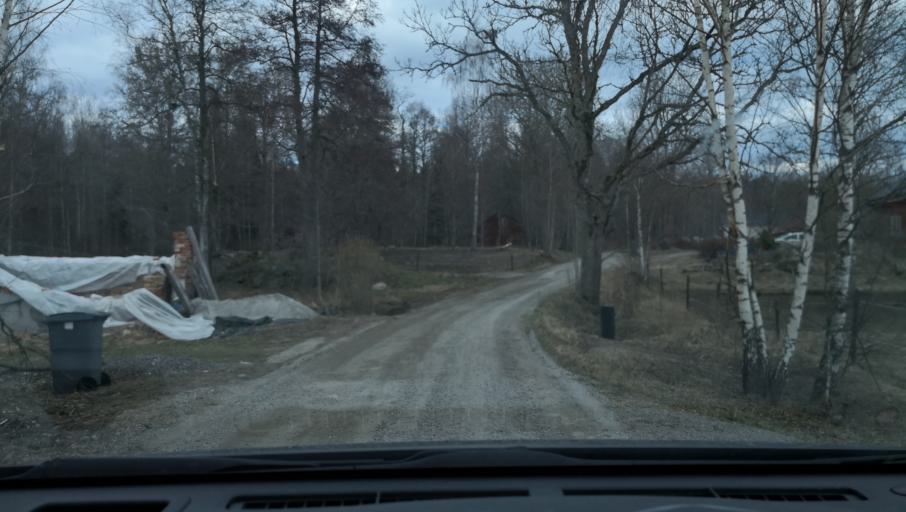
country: SE
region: Soedermanland
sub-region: Katrineholms Kommun
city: Katrineholm
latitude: 59.1304
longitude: 16.1692
